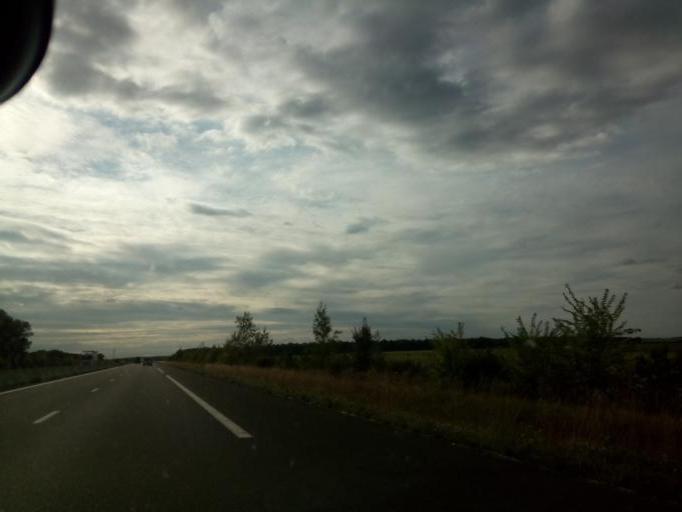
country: FR
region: Centre
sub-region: Departement d'Indre-et-Loire
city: Athee-sur-Cher
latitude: 47.2944
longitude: 0.9454
